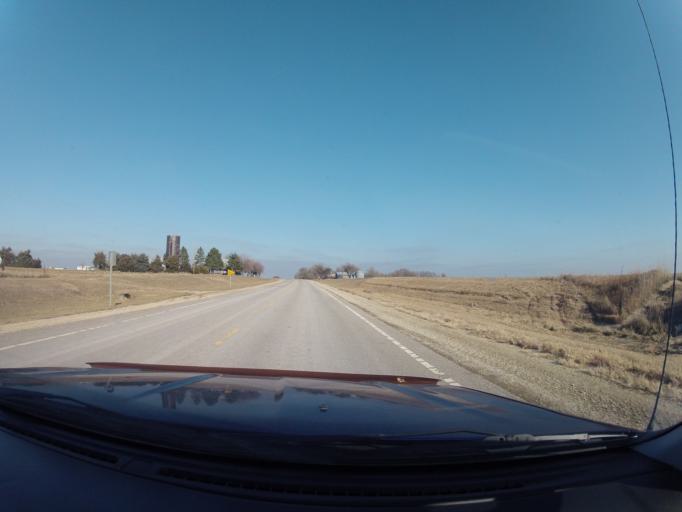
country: US
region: Kansas
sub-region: Marshall County
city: Blue Rapids
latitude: 39.5928
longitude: -96.7500
